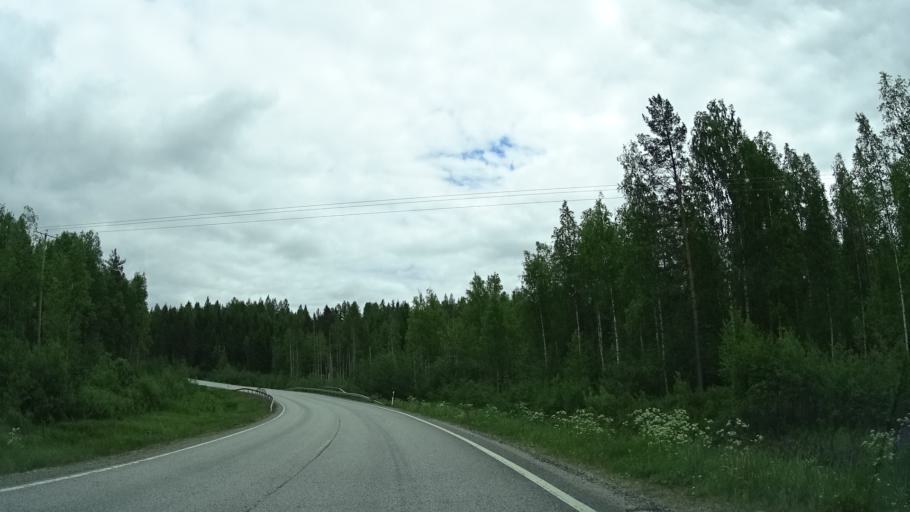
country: FI
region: Central Finland
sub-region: Jyvaeskylae
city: Toivakka
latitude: 62.0775
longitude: 26.0372
